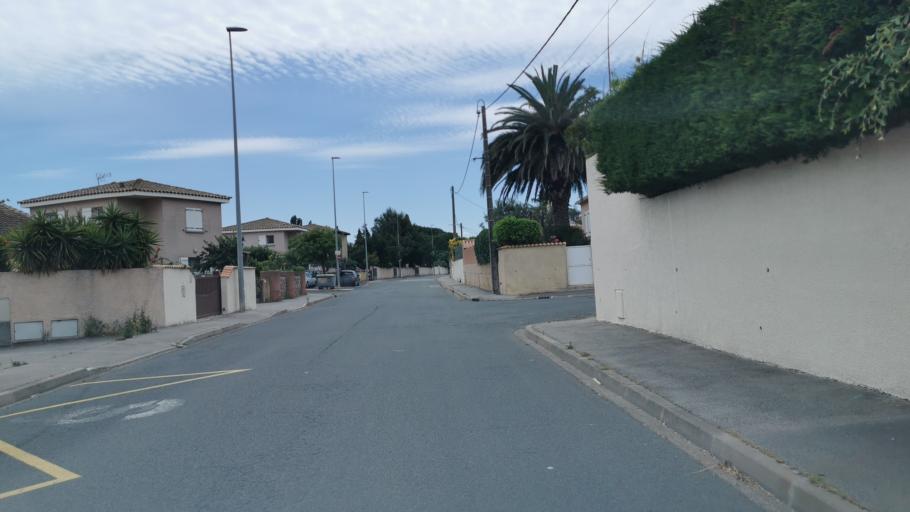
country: FR
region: Languedoc-Roussillon
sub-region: Departement de l'Aude
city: Narbonne
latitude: 43.1962
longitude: 3.0188
